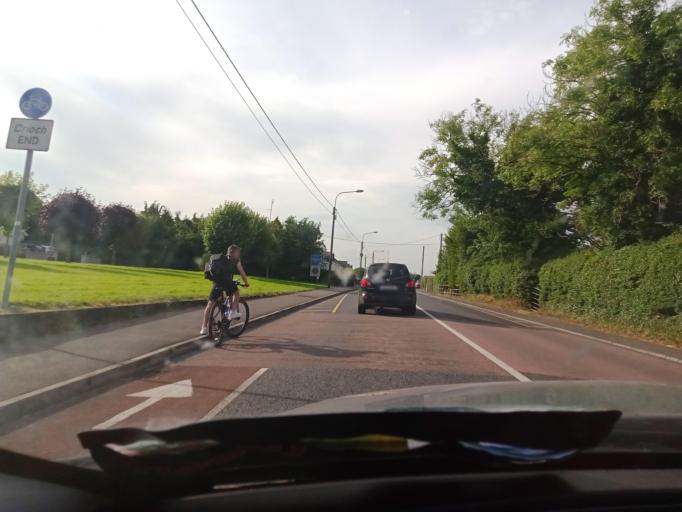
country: IE
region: Ulster
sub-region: An Cabhan
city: Cavan
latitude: 53.9806
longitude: -7.3562
